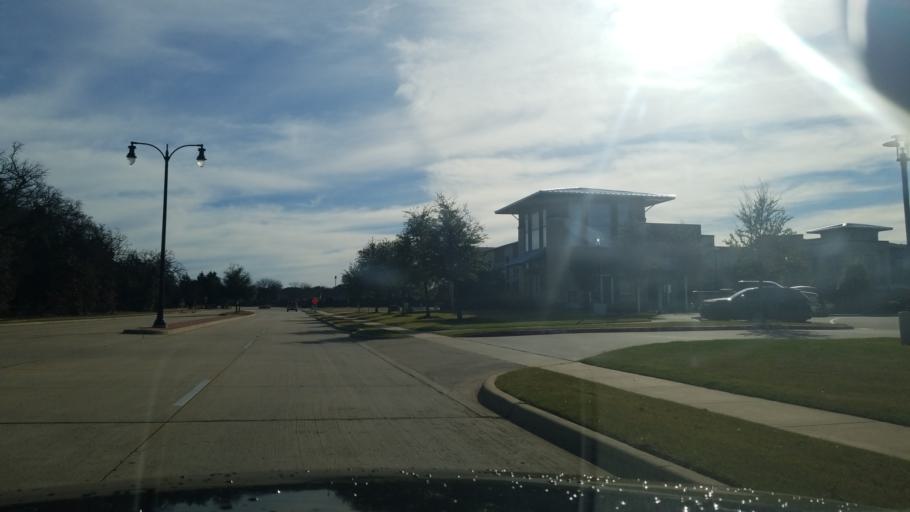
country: US
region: Texas
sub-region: Denton County
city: Corinth
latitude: 33.1465
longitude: -97.0617
